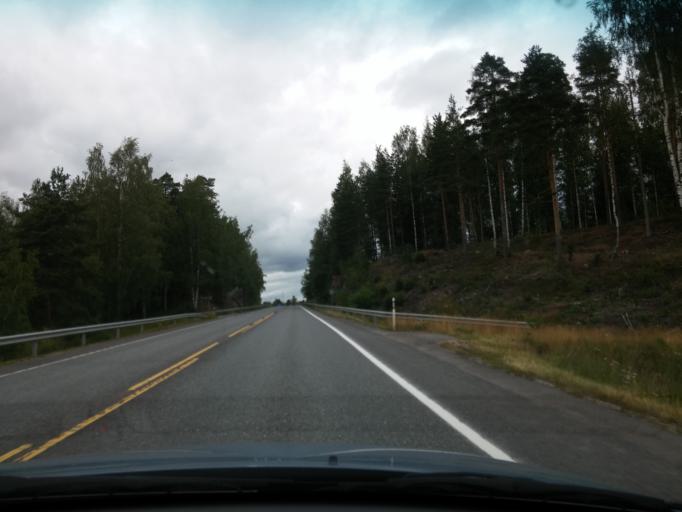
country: FI
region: Uusimaa
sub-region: Porvoo
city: Askola
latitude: 60.4905
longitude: 25.5565
